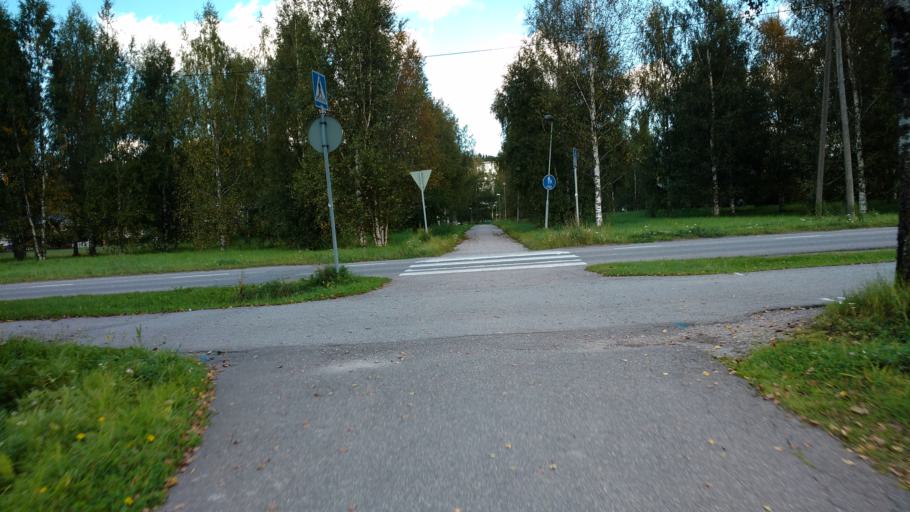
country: FI
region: Varsinais-Suomi
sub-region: Salo
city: Salo
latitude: 60.3809
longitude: 23.1486
